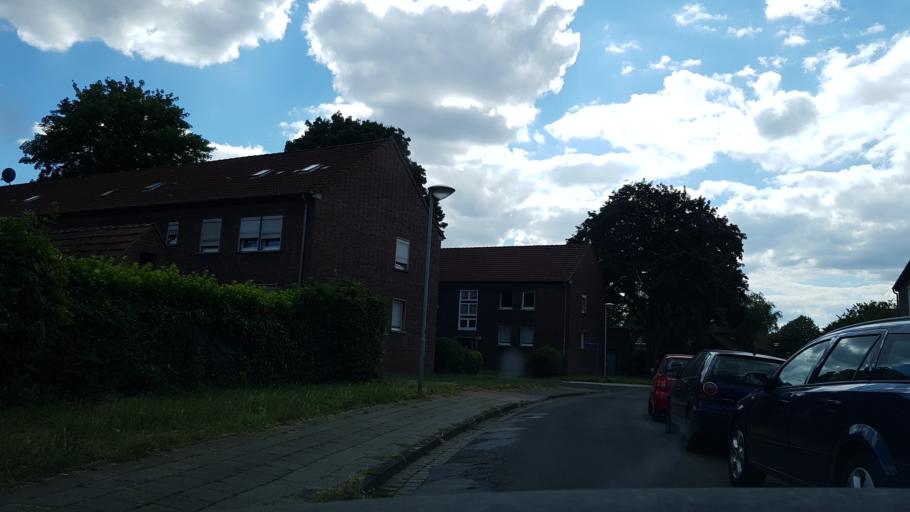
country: DE
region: North Rhine-Westphalia
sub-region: Regierungsbezirk Dusseldorf
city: Moers
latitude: 51.4422
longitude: 6.5710
